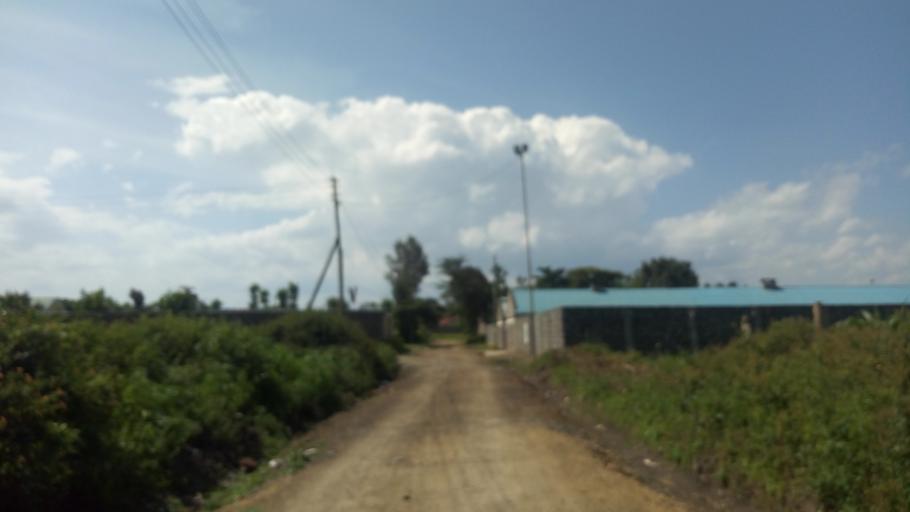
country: KE
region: Nakuru
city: Nakuru
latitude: -0.2772
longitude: 36.1193
